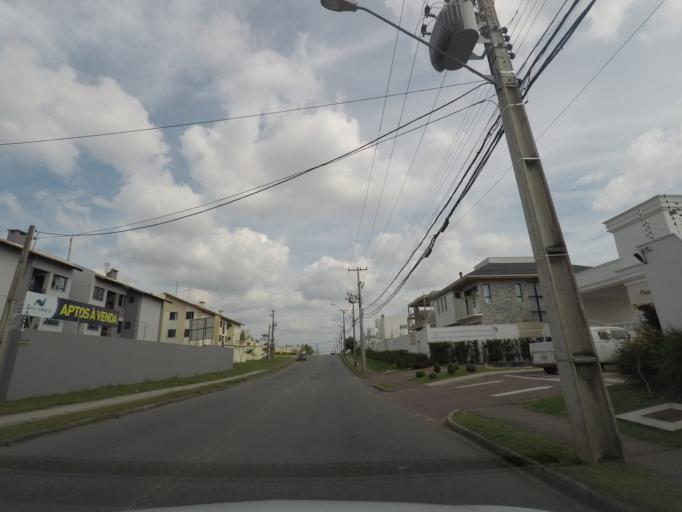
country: BR
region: Parana
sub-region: Sao Jose Dos Pinhais
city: Sao Jose dos Pinhais
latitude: -25.4860
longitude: -49.2133
